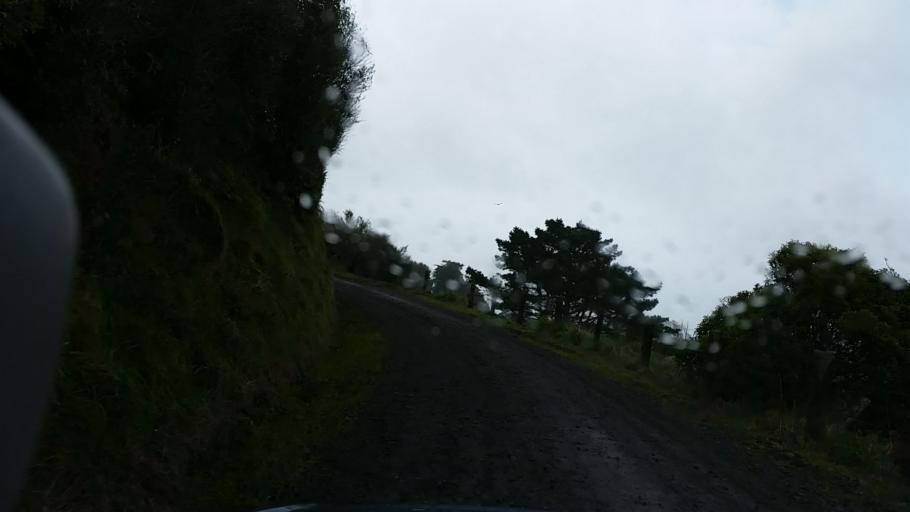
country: NZ
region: Taranaki
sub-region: South Taranaki District
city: Eltham
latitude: -39.2810
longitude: 174.3351
